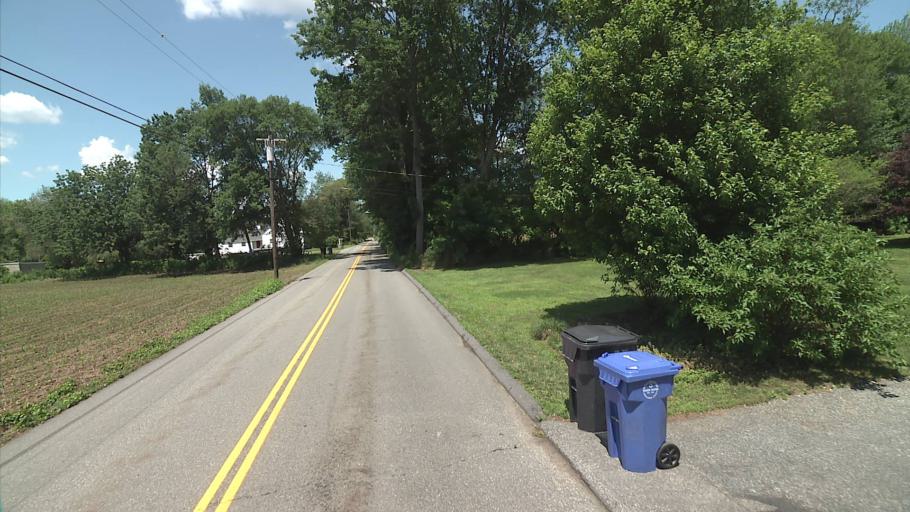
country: US
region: Connecticut
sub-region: New London County
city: Jewett City
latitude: 41.6104
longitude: -71.9303
